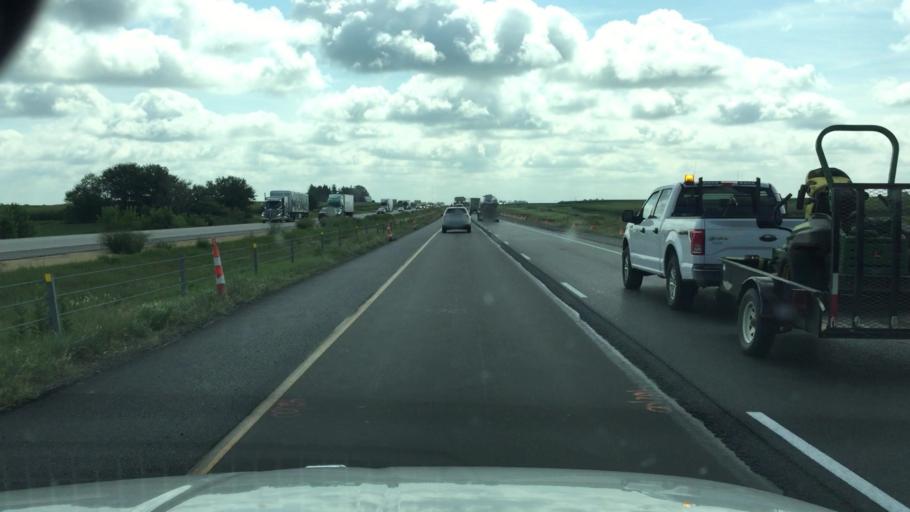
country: US
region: Iowa
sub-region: Scott County
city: Walcott
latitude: 41.6070
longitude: -90.7368
